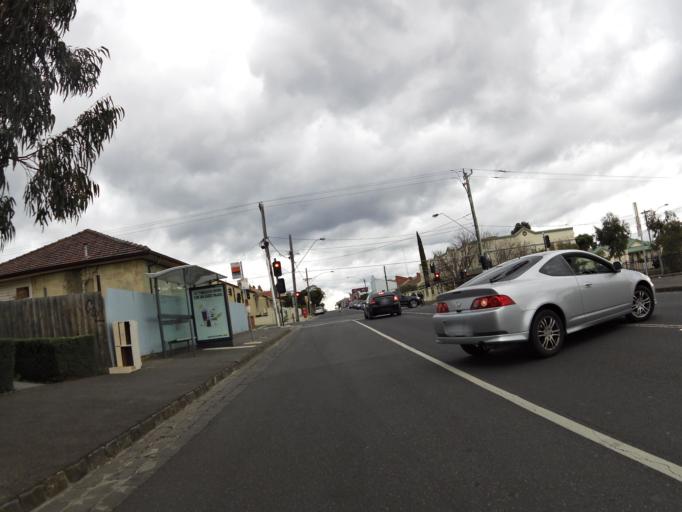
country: AU
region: Victoria
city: Brunswick West
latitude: -37.7656
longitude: 144.9498
